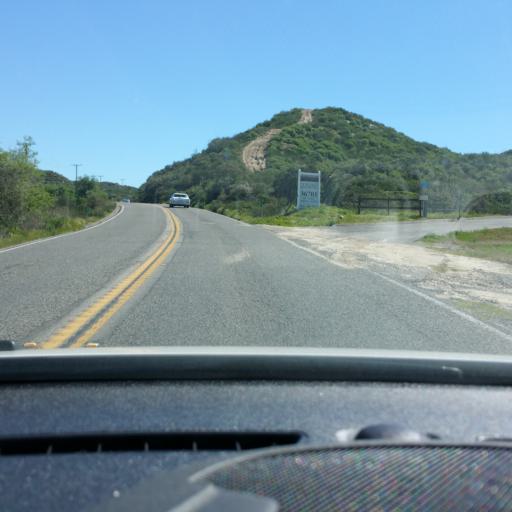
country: US
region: California
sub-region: Riverside County
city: Temecula
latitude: 33.4711
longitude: -117.0170
